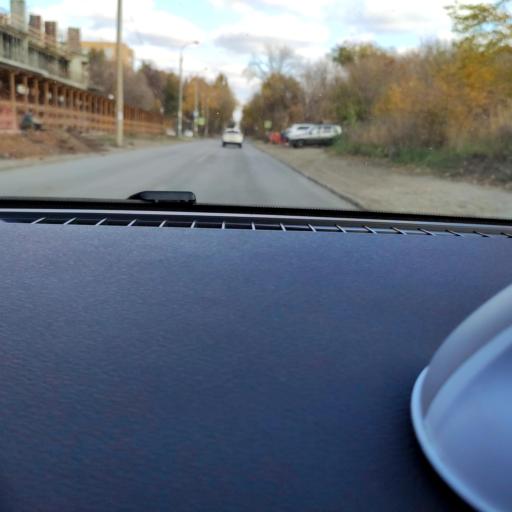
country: RU
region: Samara
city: Samara
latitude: 53.2226
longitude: 50.2055
